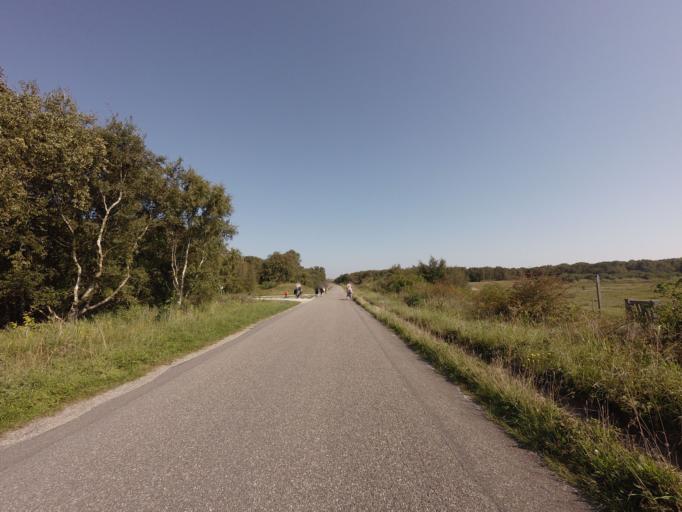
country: NL
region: Friesland
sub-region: Gemeente Schiermonnikoog
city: Schiermonnikoog
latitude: 53.4922
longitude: 6.1844
